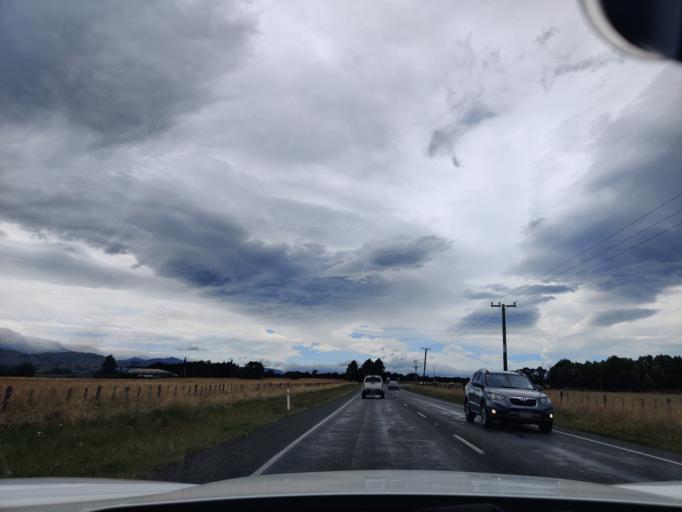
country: NZ
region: Wellington
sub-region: Masterton District
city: Masterton
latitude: -41.0018
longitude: 175.5567
